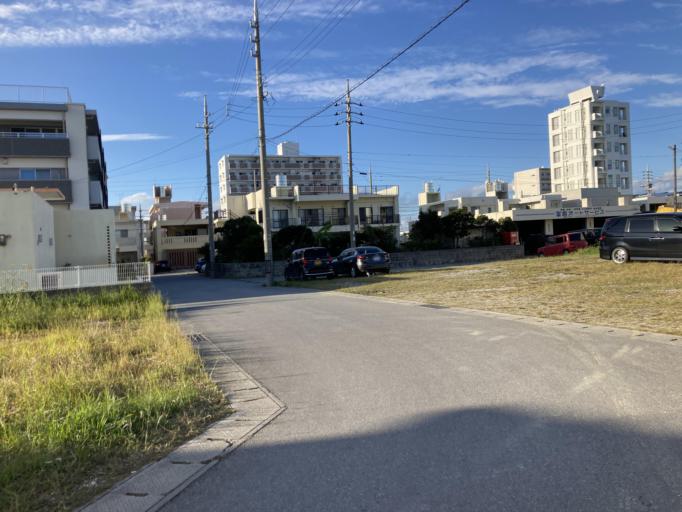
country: JP
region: Okinawa
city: Ginowan
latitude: 26.2513
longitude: 127.7759
